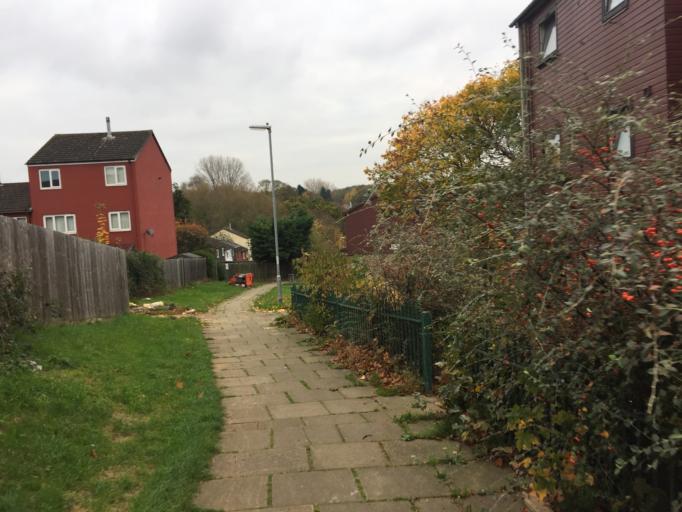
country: GB
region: England
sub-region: Northamptonshire
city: Northampton
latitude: 52.2707
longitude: -0.8366
